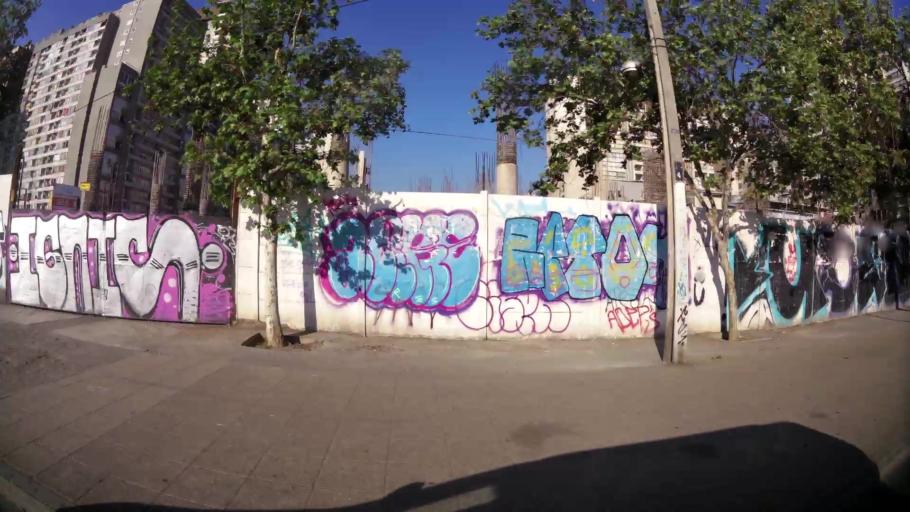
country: CL
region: Santiago Metropolitan
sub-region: Provincia de Santiago
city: Santiago
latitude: -33.4350
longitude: -70.6599
